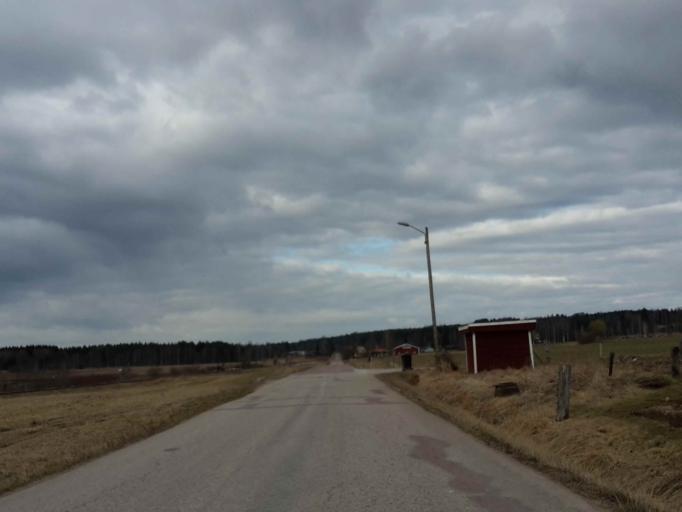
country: SE
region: Dalarna
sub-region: Orsa Kommun
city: Orsa
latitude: 61.0968
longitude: 14.6213
